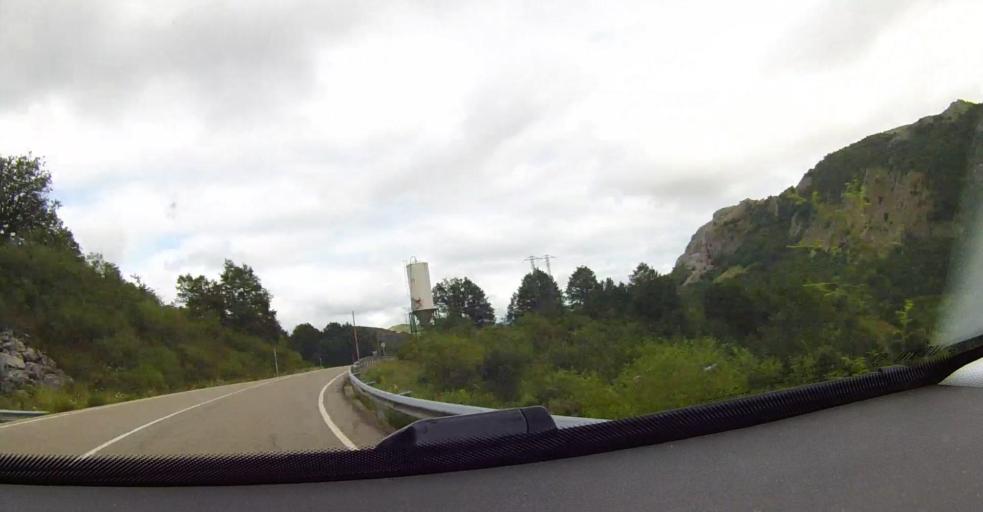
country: ES
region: Castille and Leon
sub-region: Provincia de Leon
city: Buron
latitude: 43.0170
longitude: -5.0296
